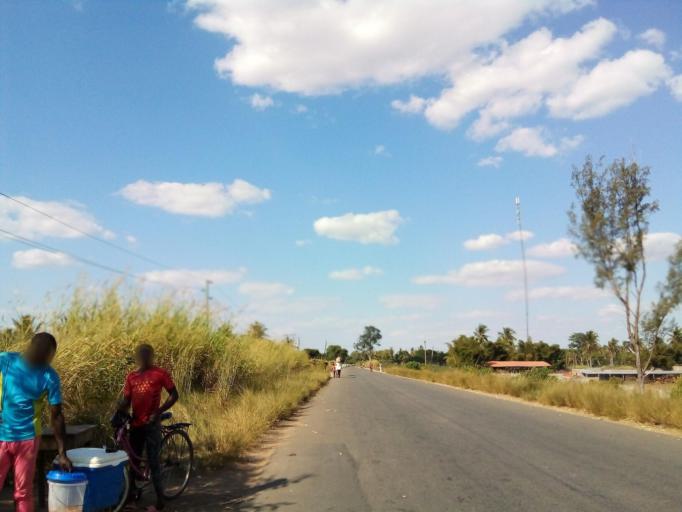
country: MZ
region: Zambezia
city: Quelimane
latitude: -17.5782
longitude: 36.6984
